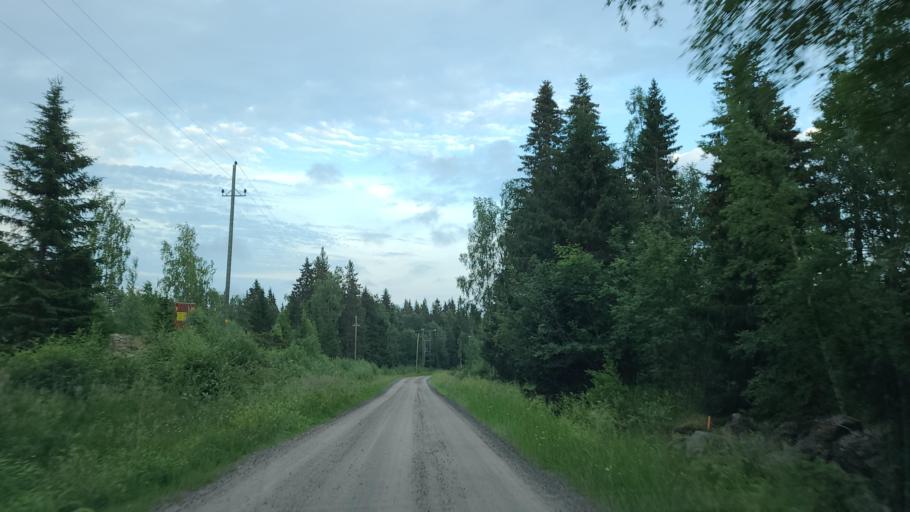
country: FI
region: Ostrobothnia
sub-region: Vaasa
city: Replot
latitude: 63.3150
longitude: 21.1587
